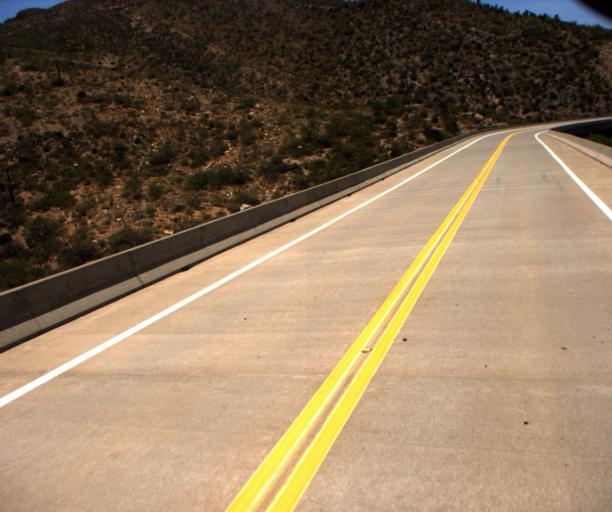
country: US
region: Arizona
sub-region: Gila County
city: Tonto Basin
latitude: 33.6750
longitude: -111.1591
